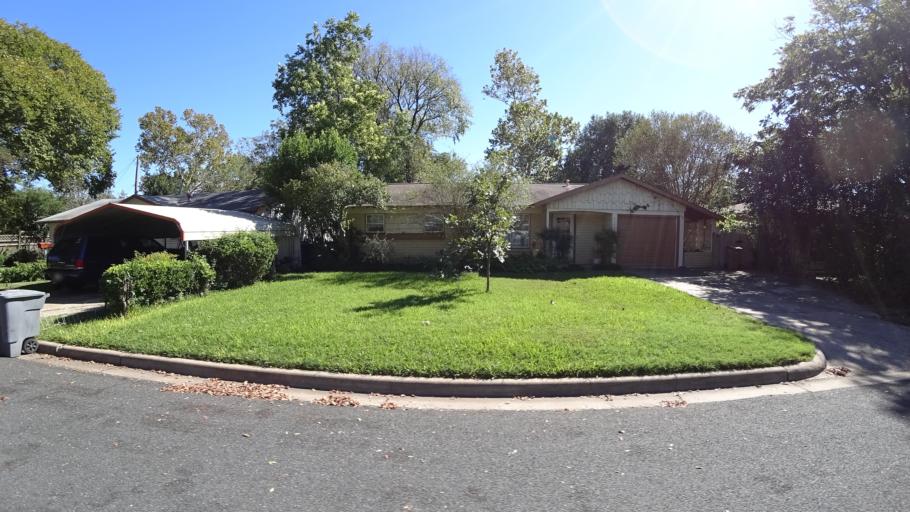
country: US
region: Texas
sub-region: Travis County
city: Rollingwood
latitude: 30.2222
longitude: -97.7882
